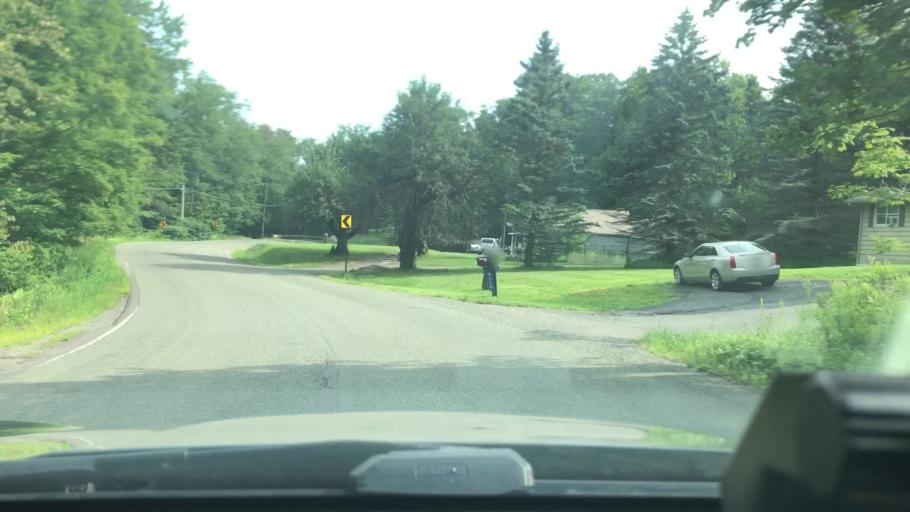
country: US
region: Pennsylvania
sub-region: Lackawanna County
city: Moscow
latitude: 41.2400
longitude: -75.4846
